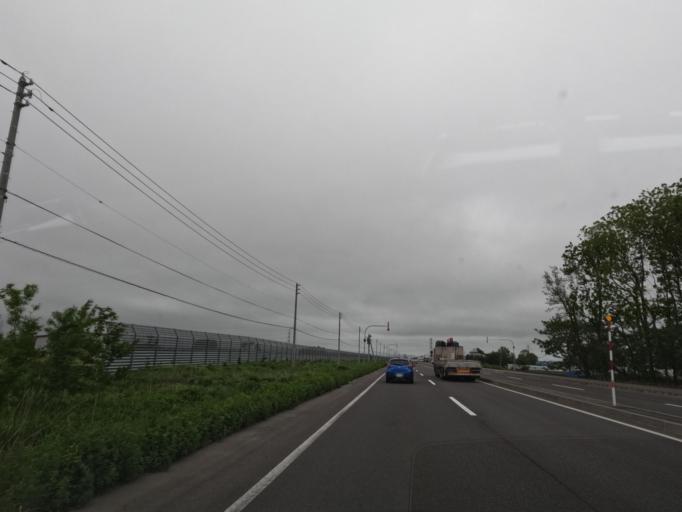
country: JP
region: Hokkaido
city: Ebetsu
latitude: 43.1519
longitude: 141.5178
